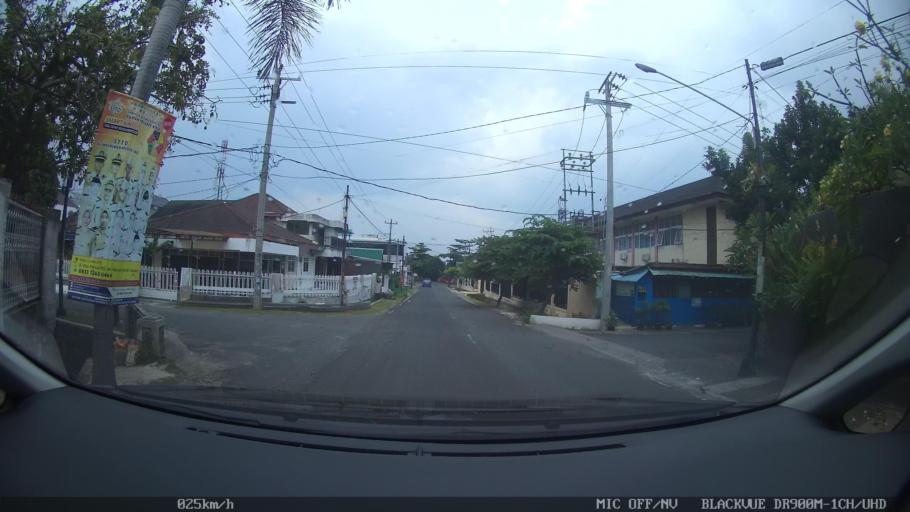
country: ID
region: Lampung
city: Bandarlampung
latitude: -5.4269
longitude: 105.2733
